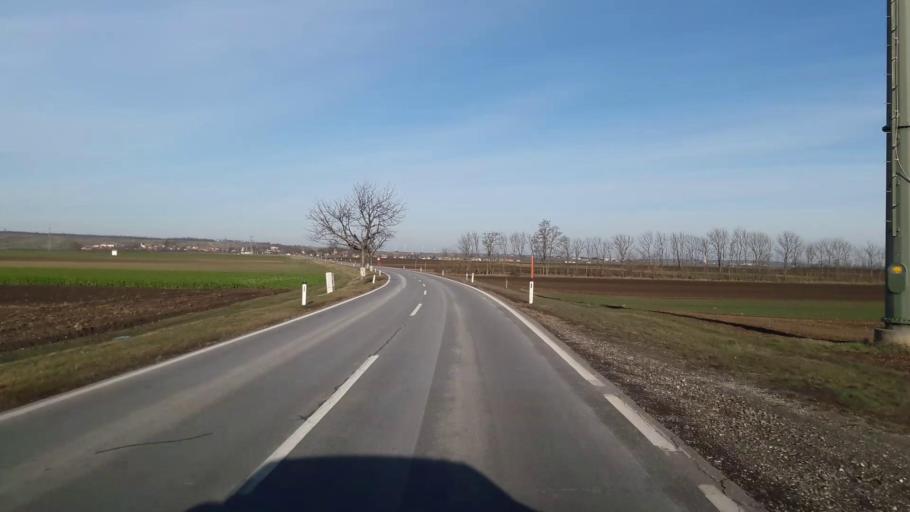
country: AT
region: Lower Austria
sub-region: Politischer Bezirk Mistelbach
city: Bockfliess
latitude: 48.3349
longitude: 16.5923
